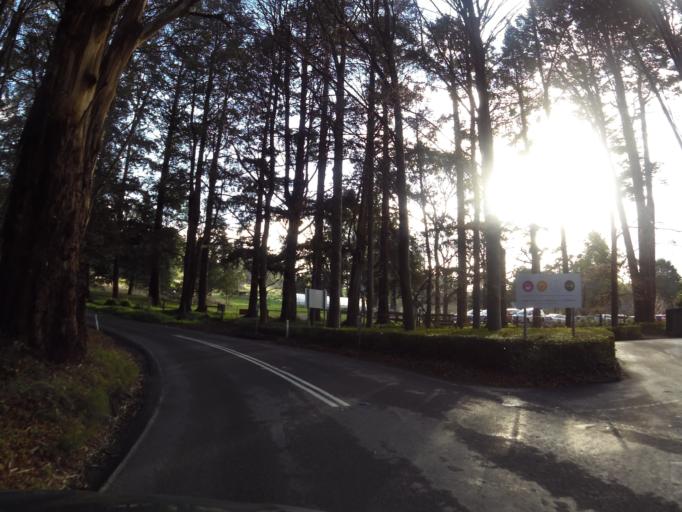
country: AU
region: Victoria
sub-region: Yarra Ranges
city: Kallista
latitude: -37.8763
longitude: 145.3554
